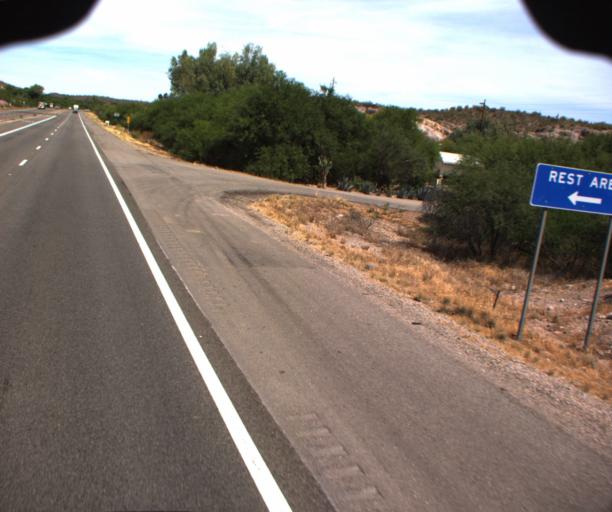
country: US
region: Arizona
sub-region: Maricopa County
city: Wickenburg
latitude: 33.9076
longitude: -112.6737
